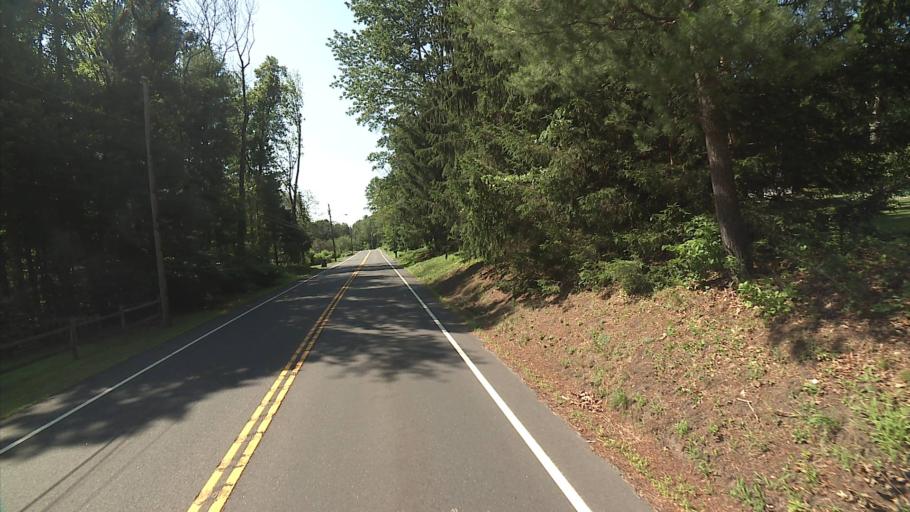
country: US
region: Connecticut
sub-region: Litchfield County
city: Terryville
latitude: 41.6982
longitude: -73.0066
